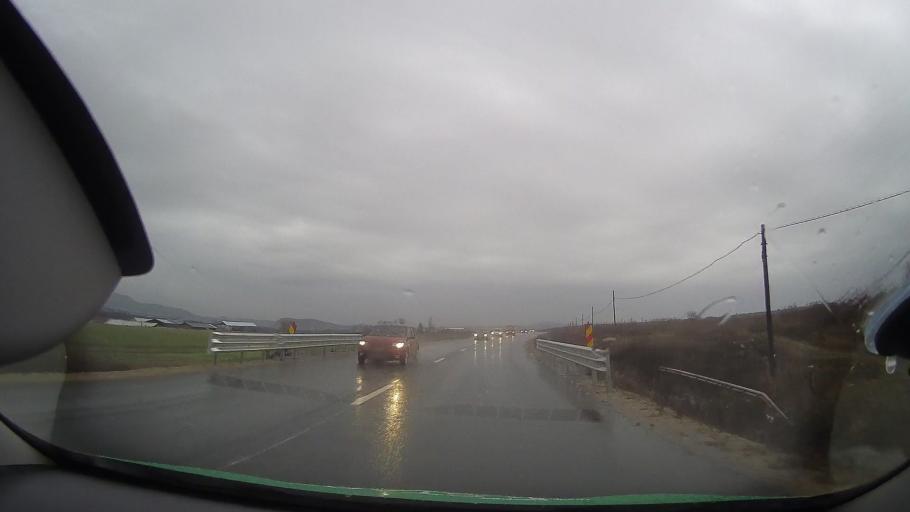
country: RO
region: Bihor
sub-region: Municipiul Beius
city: Beius
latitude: 46.6743
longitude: 22.3252
